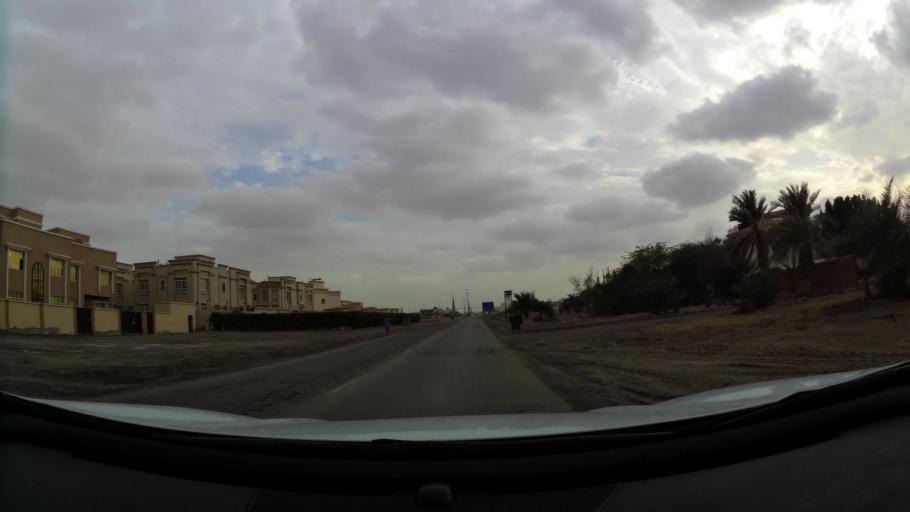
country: AE
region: Abu Dhabi
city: Abu Dhabi
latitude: 24.3515
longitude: 54.5531
